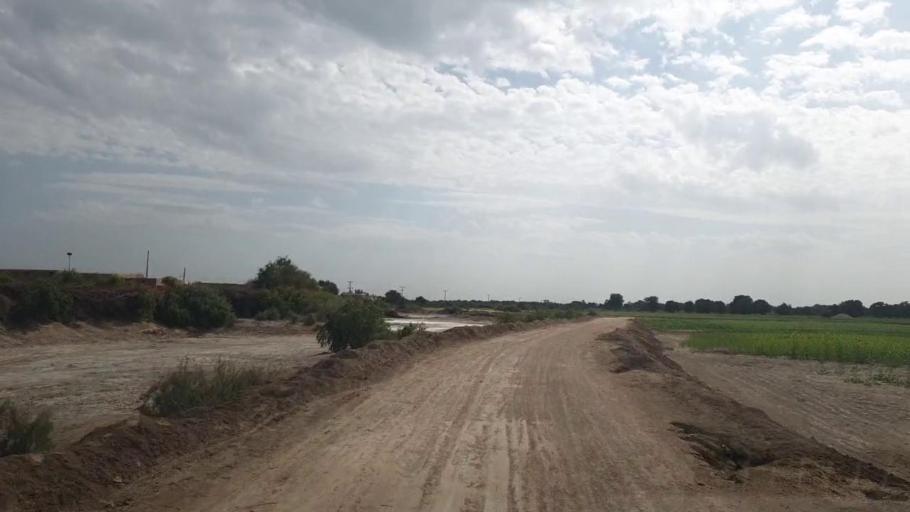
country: PK
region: Sindh
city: Hala
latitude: 25.9233
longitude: 68.4287
